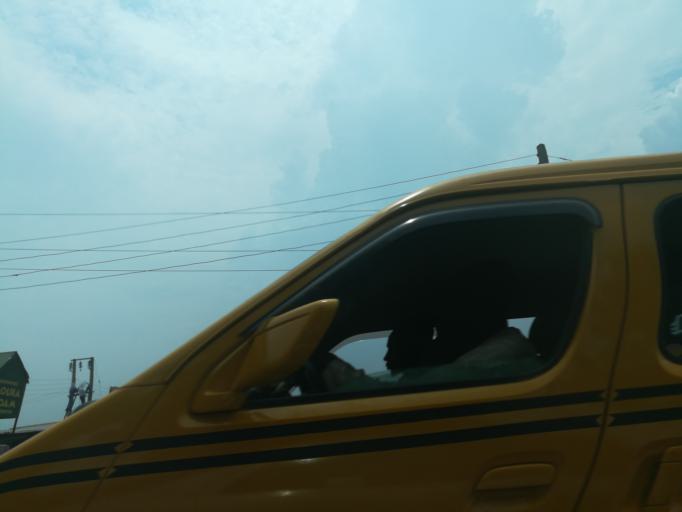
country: NG
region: Lagos
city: Ikorodu
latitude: 6.6062
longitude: 3.5860
